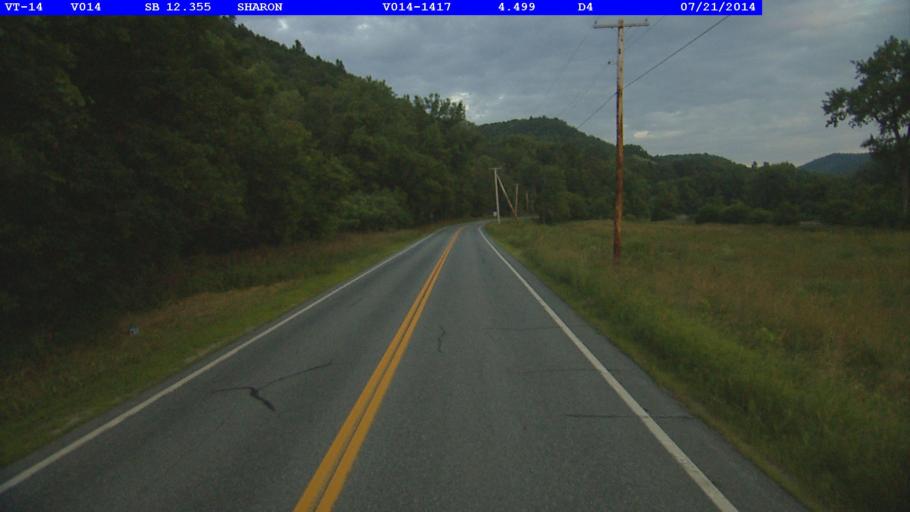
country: US
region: Vermont
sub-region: Windsor County
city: Woodstock
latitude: 43.7802
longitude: -72.4465
